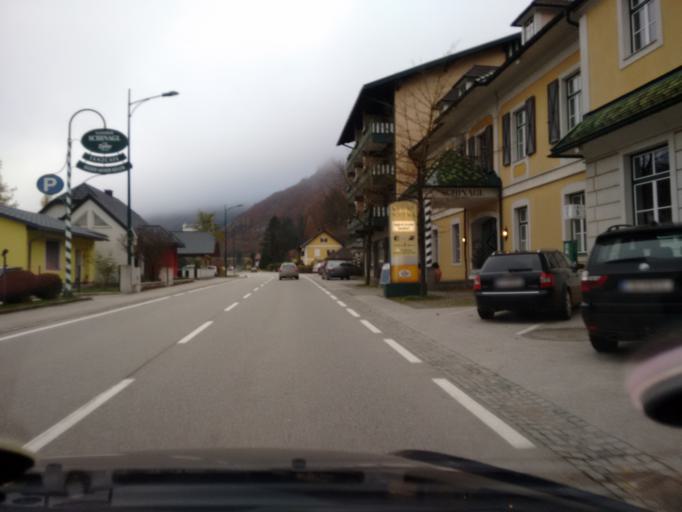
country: AT
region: Upper Austria
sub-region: Politischer Bezirk Kirchdorf an der Krems
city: Micheldorf in Oberoesterreich
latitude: 47.8322
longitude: 14.1575
